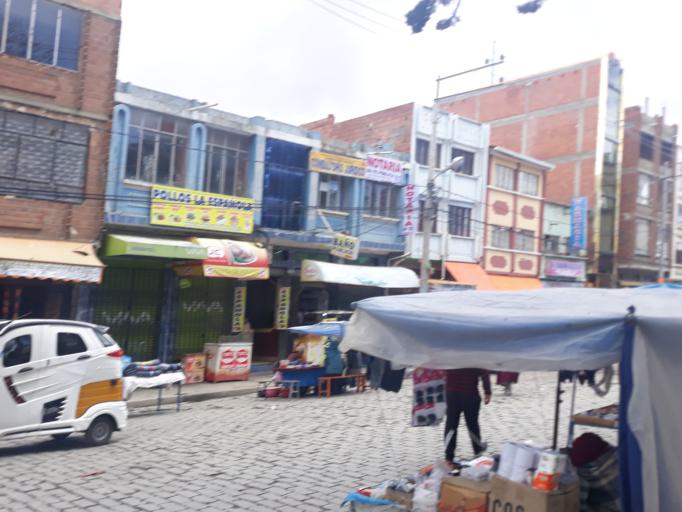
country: BO
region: La Paz
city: Achacachi
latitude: -16.0441
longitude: -68.6847
